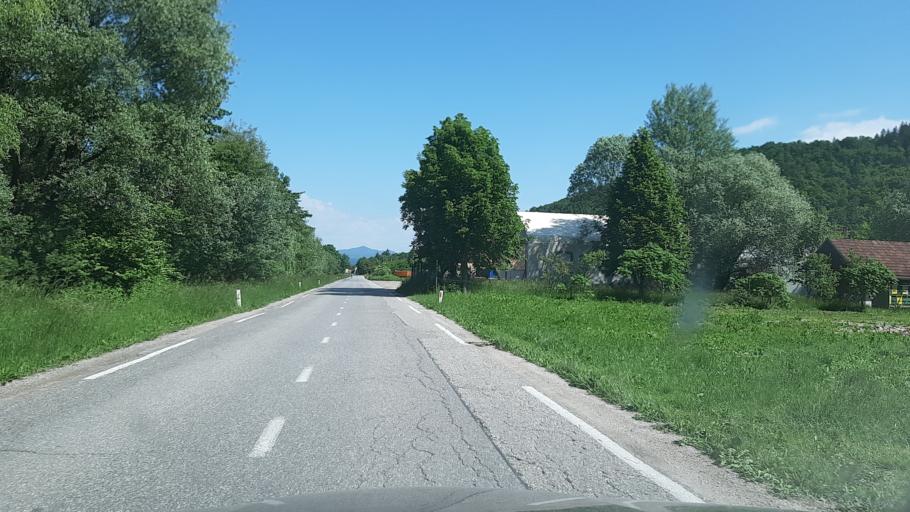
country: SI
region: Borovnica
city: Borovnica
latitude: 45.9268
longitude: 14.3645
